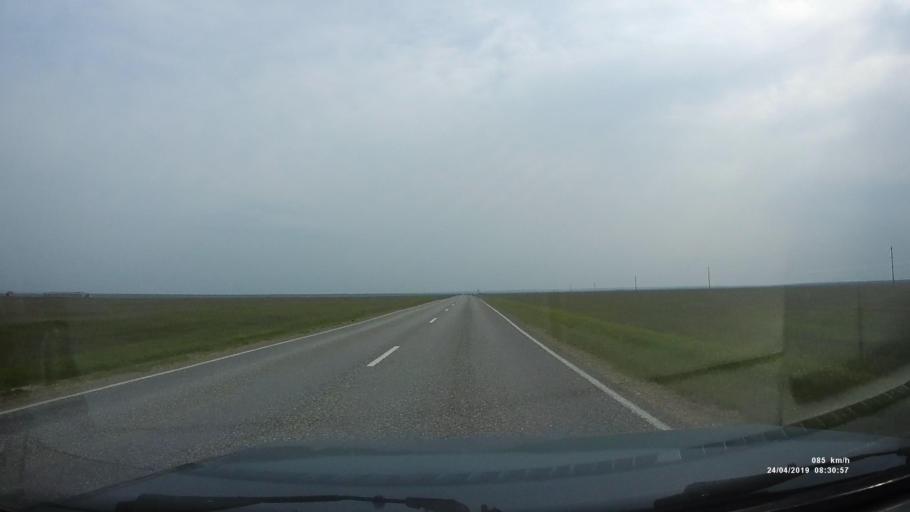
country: RU
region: Kalmykiya
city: Priyutnoye
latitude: 46.1633
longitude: 43.8531
